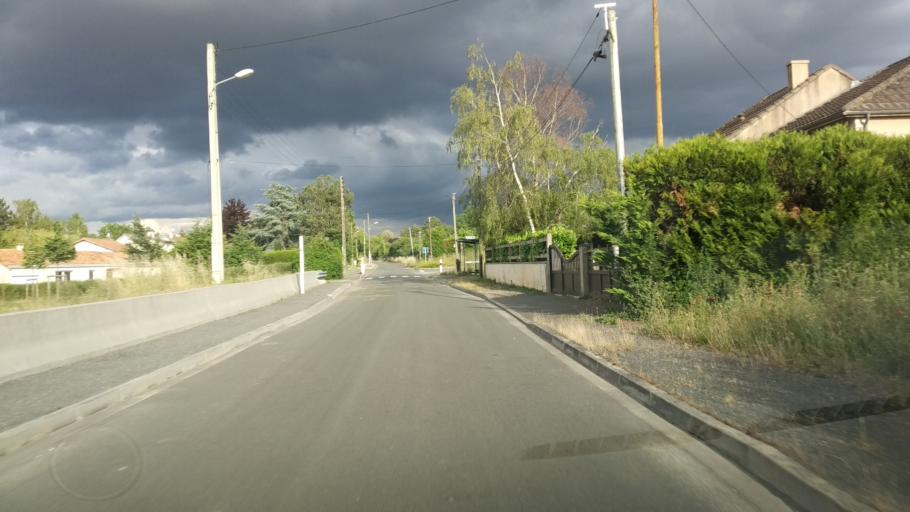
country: FR
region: Poitou-Charentes
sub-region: Departement de la Vienne
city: Migne-Auxances
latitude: 46.6262
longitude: 0.3415
